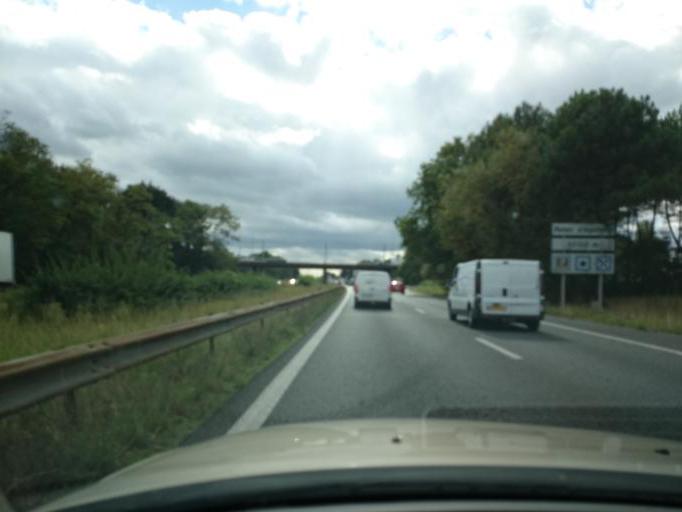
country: FR
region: Aquitaine
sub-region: Departement de la Gironde
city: Le Haillan
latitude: 44.8589
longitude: -0.6611
